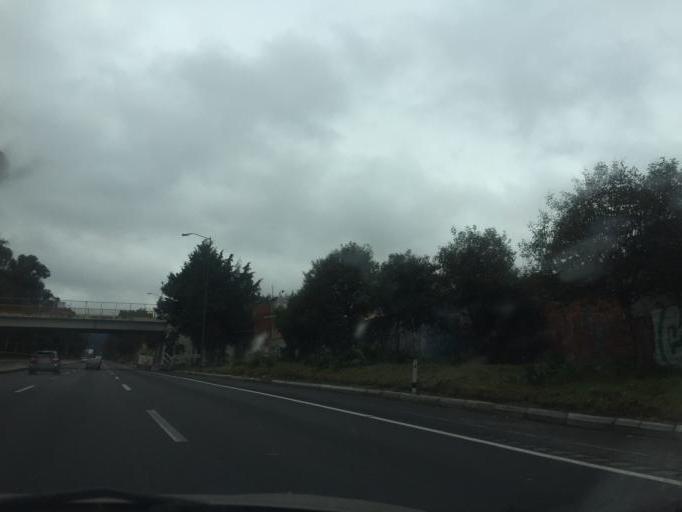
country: MX
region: Mexico City
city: Xochimilco
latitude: 19.1996
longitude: -99.1449
